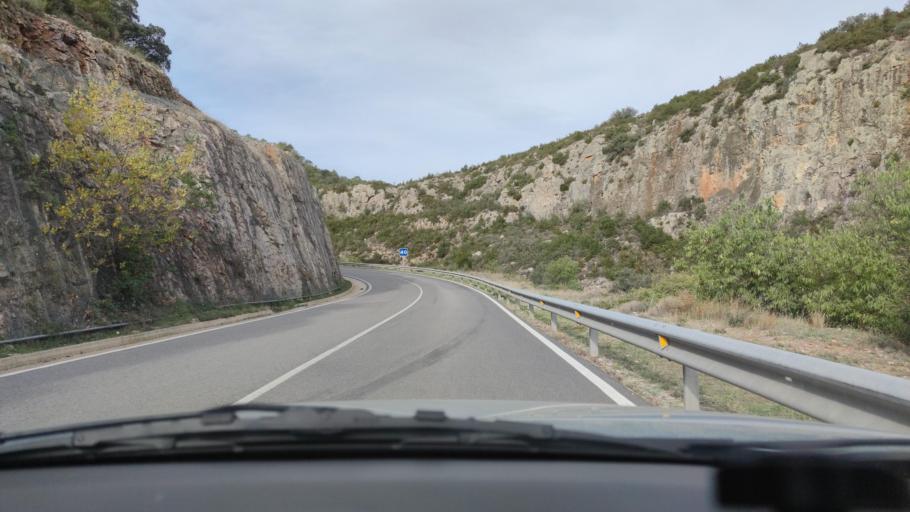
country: ES
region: Catalonia
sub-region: Provincia de Lleida
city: Artesa de Segre
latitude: 41.9324
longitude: 1.0540
